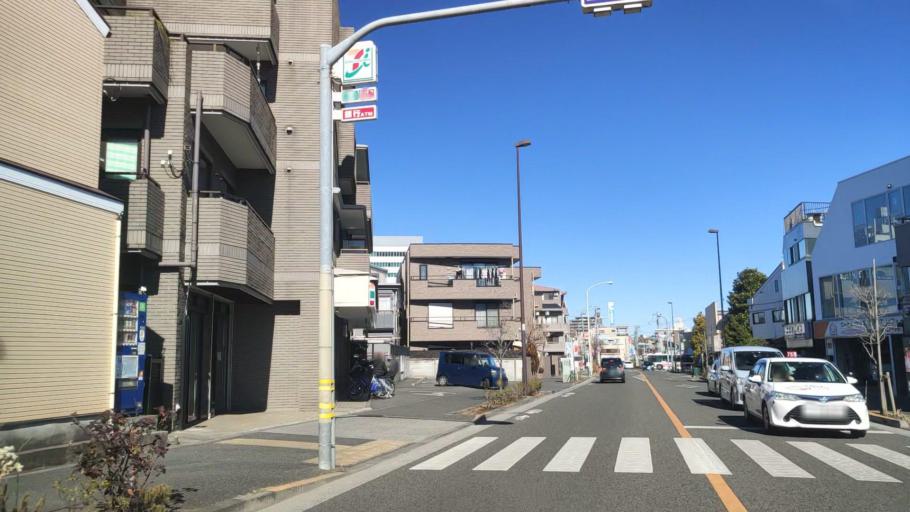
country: JP
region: Tokyo
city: Mitaka-shi
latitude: 35.6752
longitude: 139.5673
